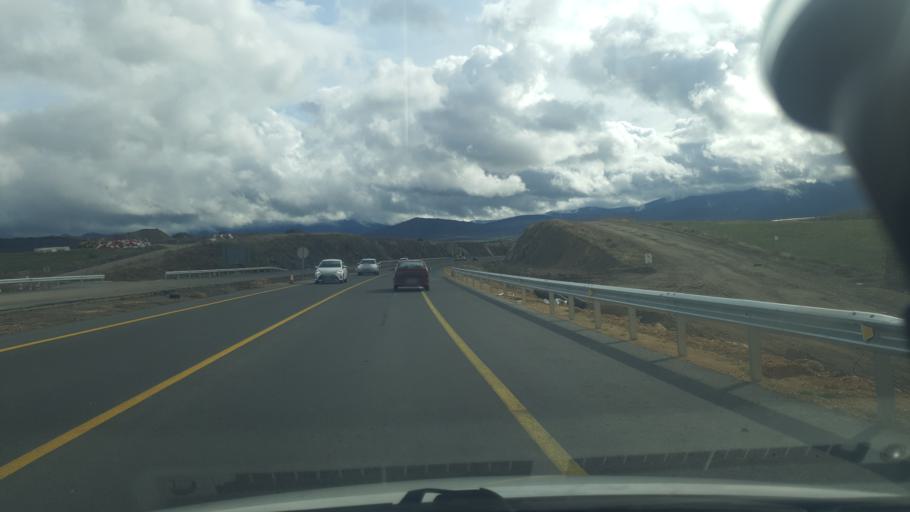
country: ES
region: Castille and Leon
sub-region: Provincia de Segovia
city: San Cristobal de Segovia
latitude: 40.9463
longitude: -4.0874
